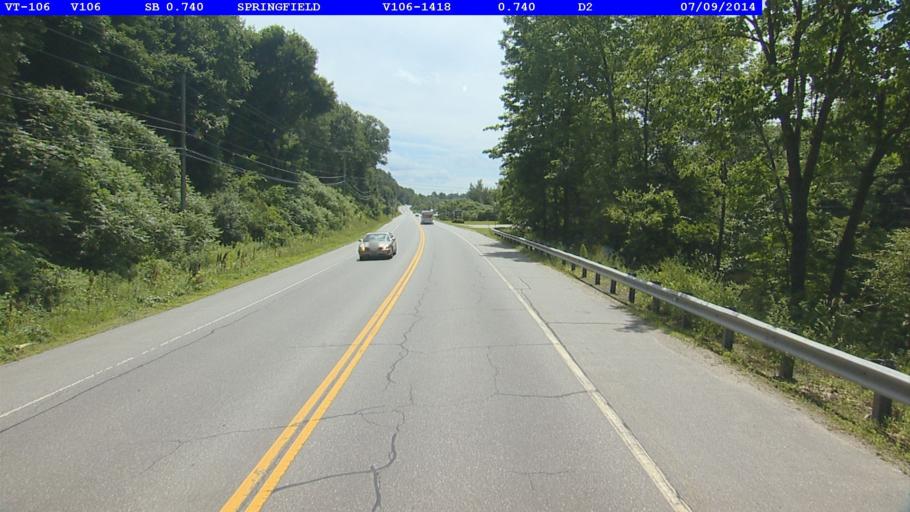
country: US
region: Vermont
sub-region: Windsor County
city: Springfield
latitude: 43.3125
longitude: -72.5003
